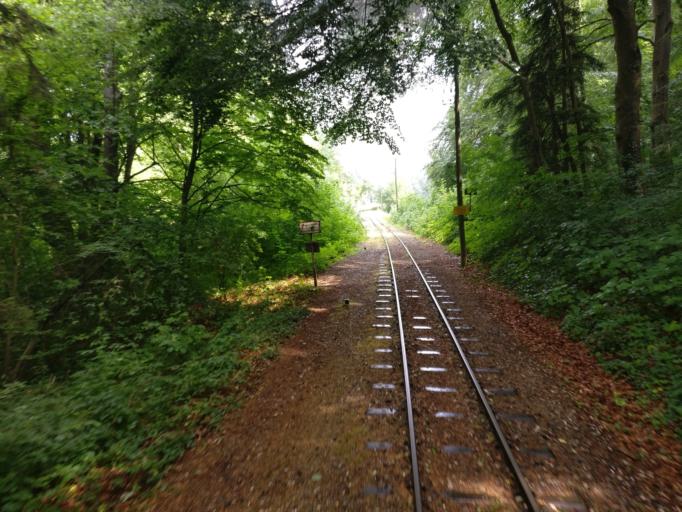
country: AT
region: Upper Austria
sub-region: Politischer Bezirk Steyr-Land
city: Sierning
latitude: 48.0480
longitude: 14.3390
